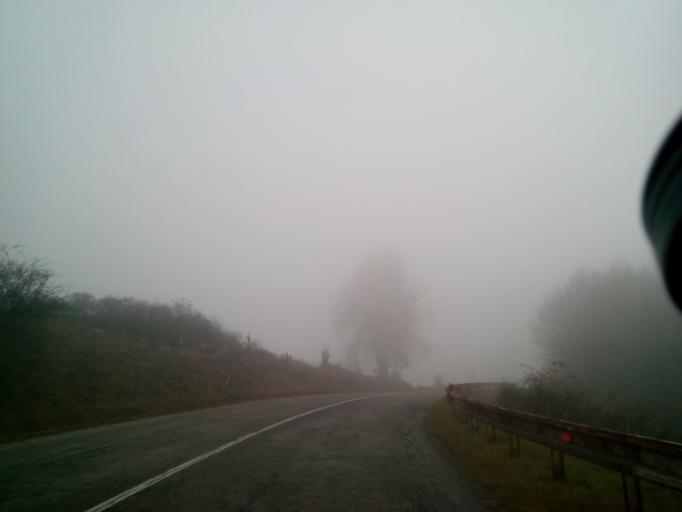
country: SK
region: Kosicky
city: Gelnica
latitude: 48.8504
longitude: 21.0310
